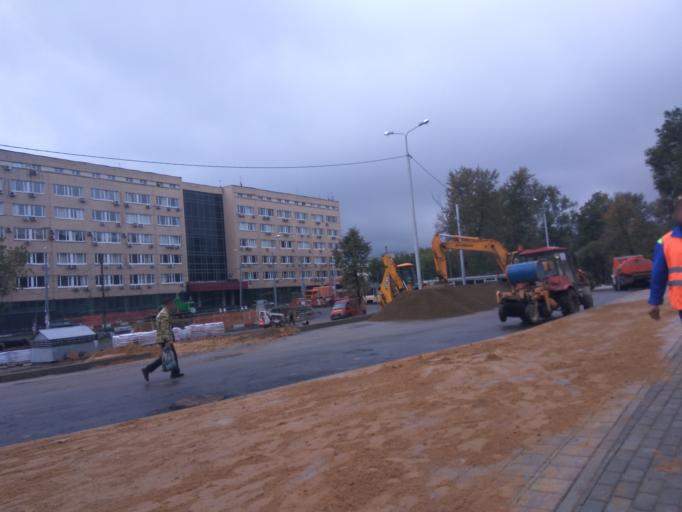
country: RU
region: Moskovskaya
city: Kozhukhovo
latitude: 55.7163
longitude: 37.6965
